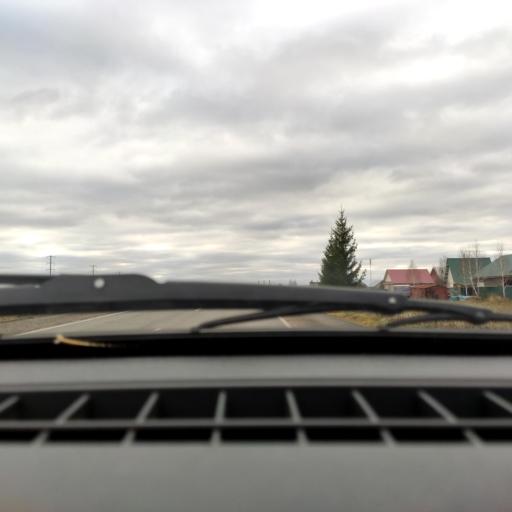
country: RU
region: Bashkortostan
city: Iglino
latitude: 54.7825
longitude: 56.2529
